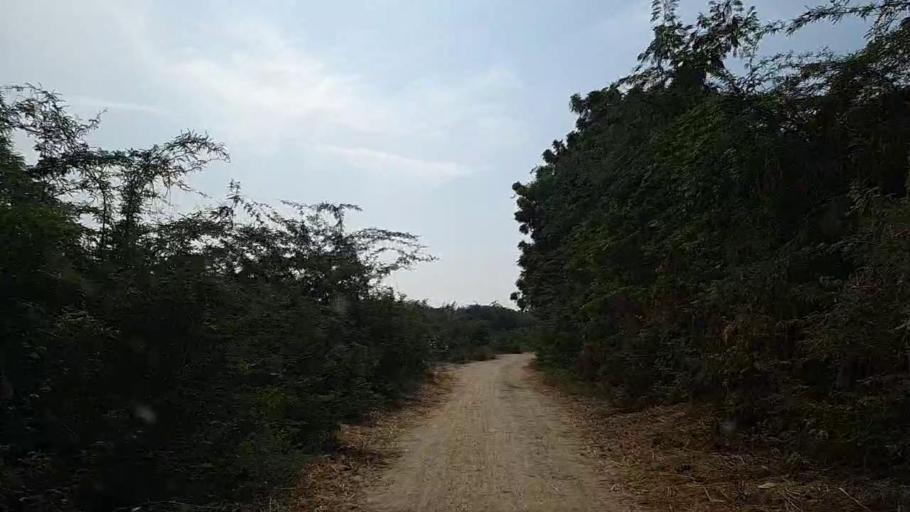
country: PK
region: Sindh
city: Daro Mehar
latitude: 24.7053
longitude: 68.1582
